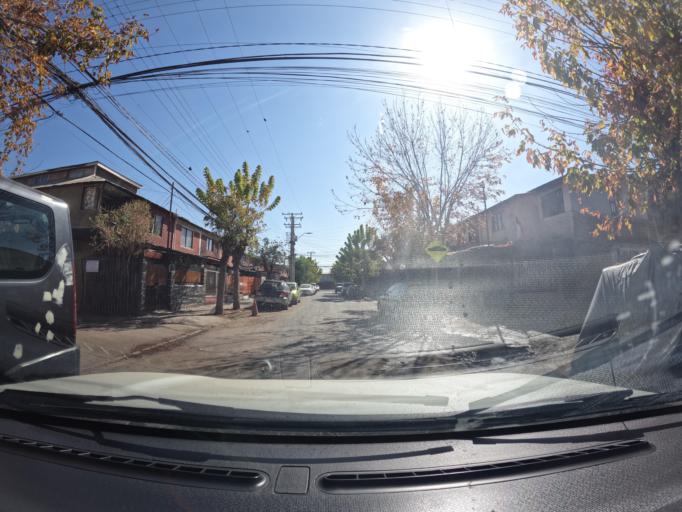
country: CL
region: Santiago Metropolitan
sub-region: Provincia de Santiago
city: Villa Presidente Frei, Nunoa, Santiago, Chile
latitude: -33.4823
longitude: -70.5637
